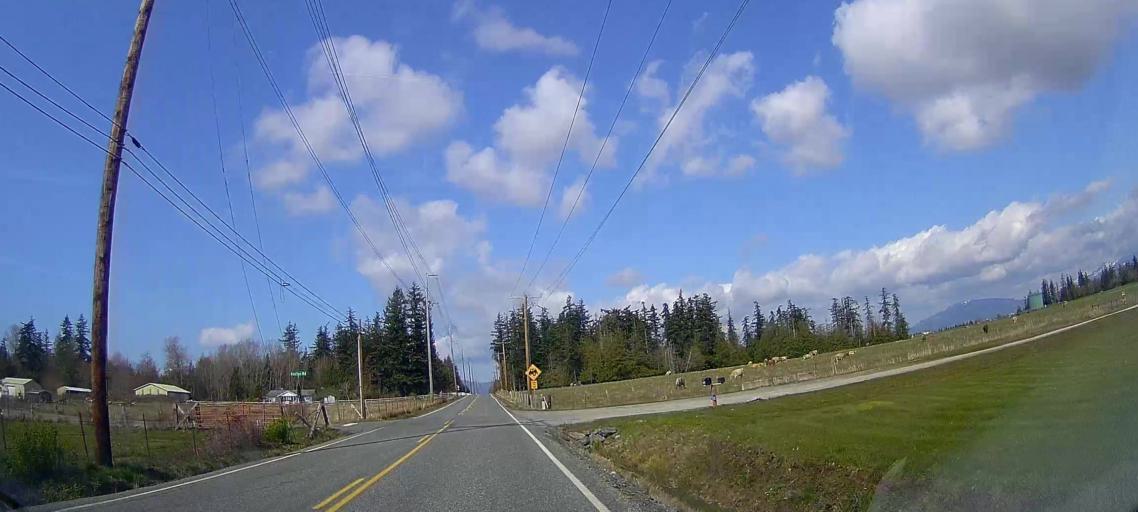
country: US
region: Washington
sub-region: Skagit County
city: Burlington
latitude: 48.4937
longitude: -122.4444
